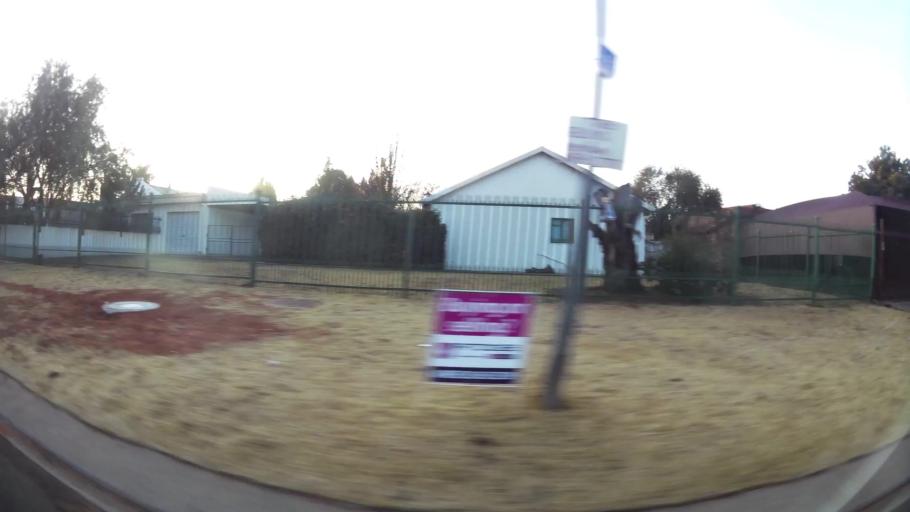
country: ZA
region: Orange Free State
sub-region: Mangaung Metropolitan Municipality
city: Bloemfontein
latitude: -29.1059
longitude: 26.1491
